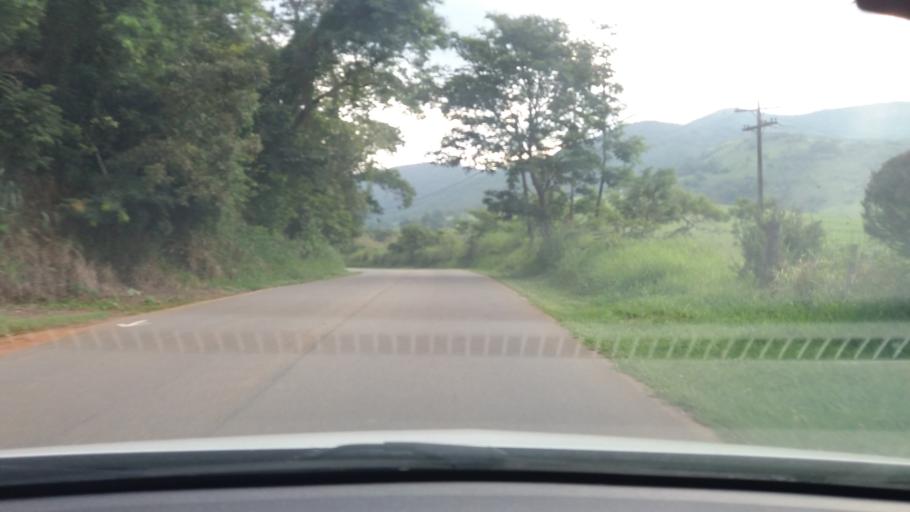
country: BR
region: Sao Paulo
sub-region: Bom Jesus Dos Perdoes
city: Bom Jesus dos Perdoes
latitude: -23.1633
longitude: -46.4769
